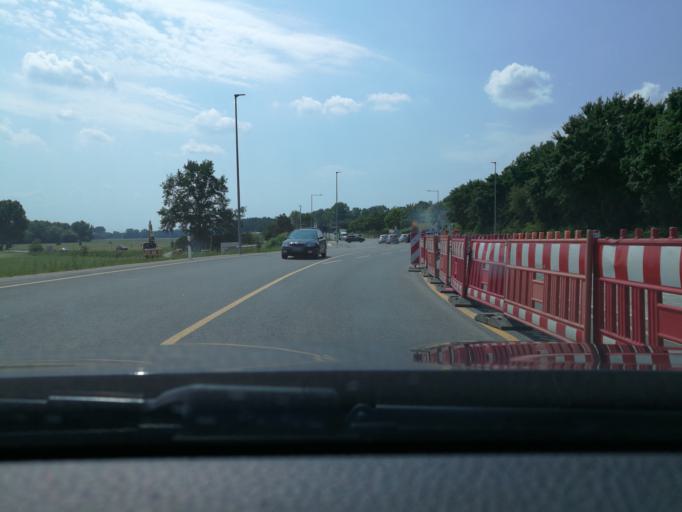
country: DE
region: Bavaria
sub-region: Regierungsbezirk Mittelfranken
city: Furth
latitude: 49.5133
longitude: 10.9644
